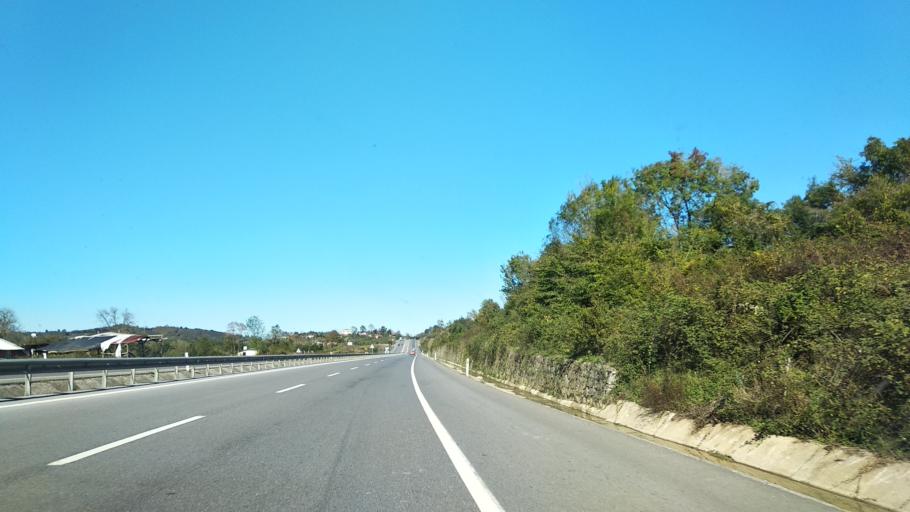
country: TR
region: Sakarya
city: Ortakoy
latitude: 41.0382
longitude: 30.6191
